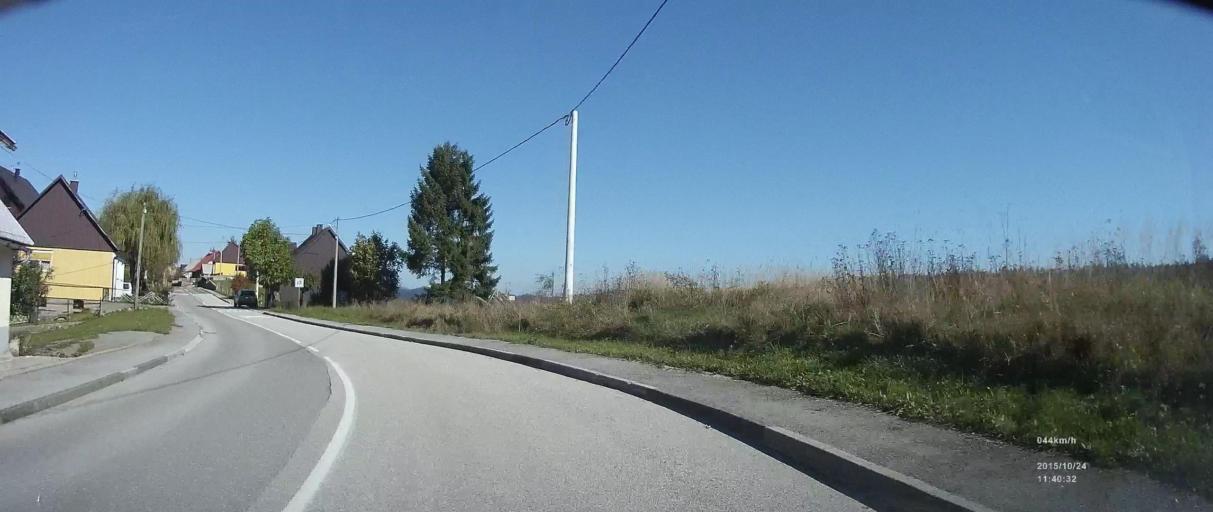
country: HR
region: Primorsko-Goranska
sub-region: Grad Delnice
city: Delnice
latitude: 45.4156
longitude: 14.7058
